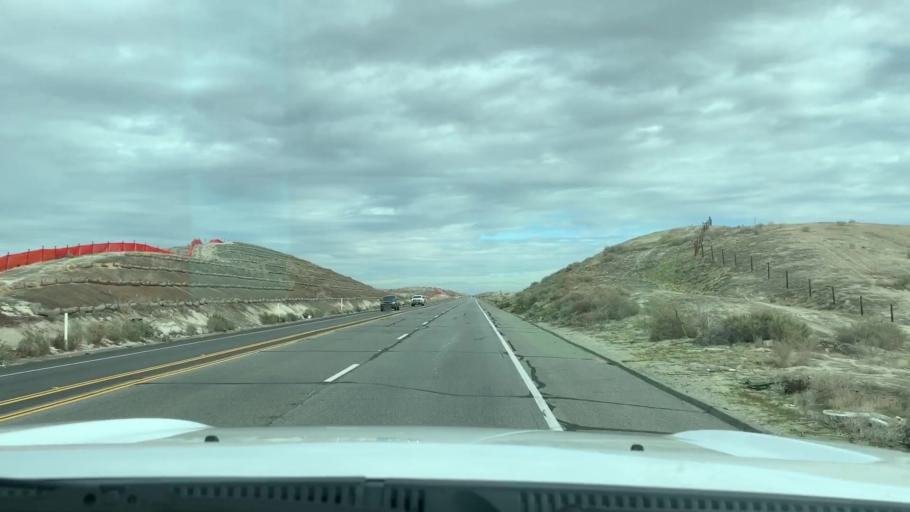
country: US
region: California
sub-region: Kern County
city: Ford City
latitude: 35.2427
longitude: -119.3530
